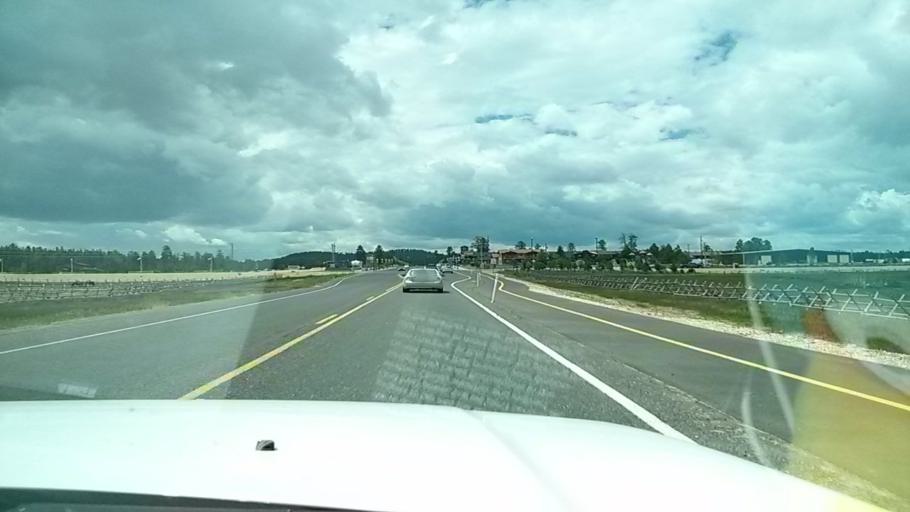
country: US
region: Utah
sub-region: Garfield County
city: Panguitch
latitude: 37.6787
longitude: -112.1552
